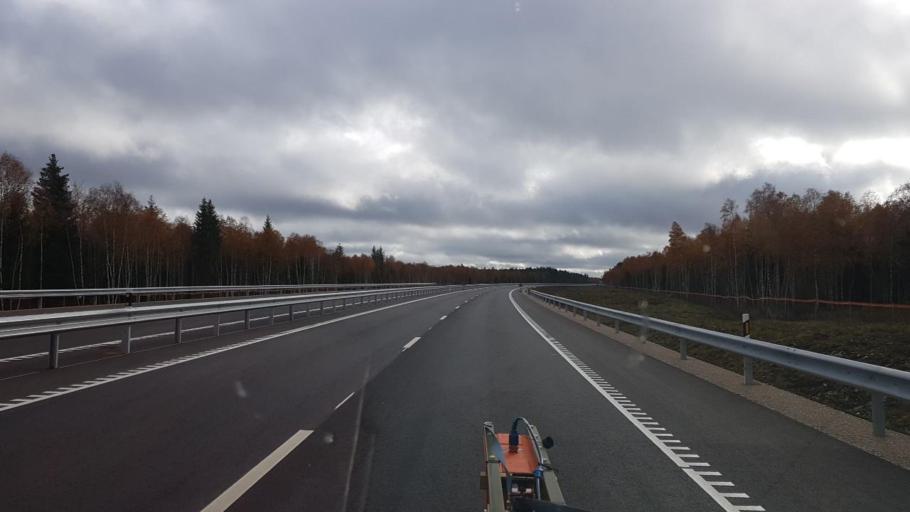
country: EE
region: Jaervamaa
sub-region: Paide linn
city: Paide
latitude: 59.0260
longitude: 25.5410
